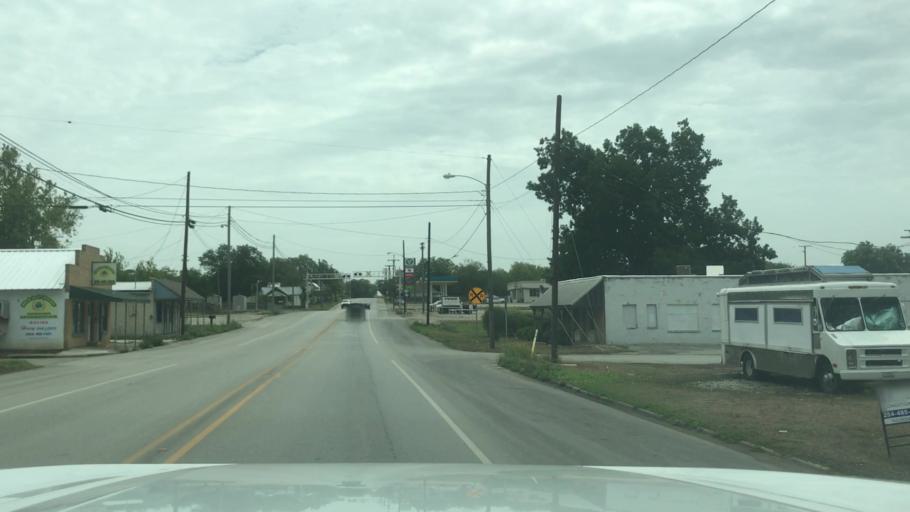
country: US
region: Texas
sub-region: Erath County
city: Dublin
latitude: 32.0846
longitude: -98.3398
